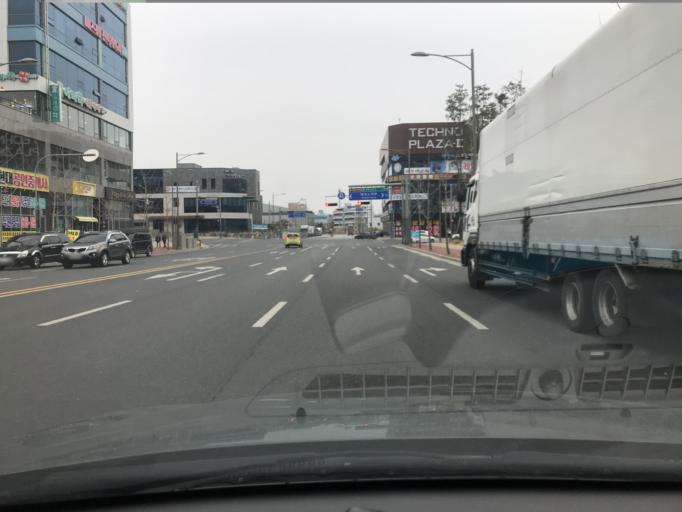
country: KR
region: Daegu
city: Hwawon
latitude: 35.6903
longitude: 128.4526
